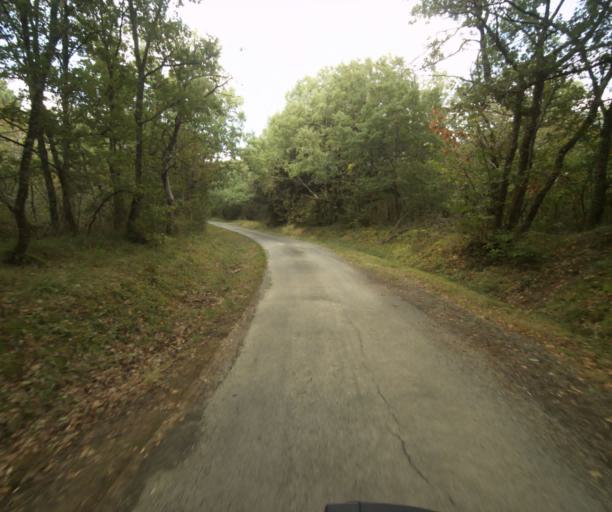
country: FR
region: Midi-Pyrenees
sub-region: Departement de la Haute-Garonne
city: Launac
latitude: 43.8292
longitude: 1.1142
